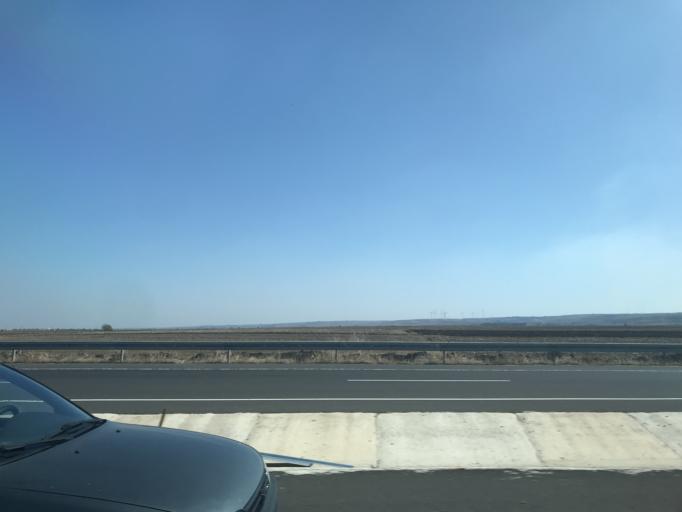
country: TR
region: Tekirdag
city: Muratli
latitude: 41.1713
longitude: 27.5366
